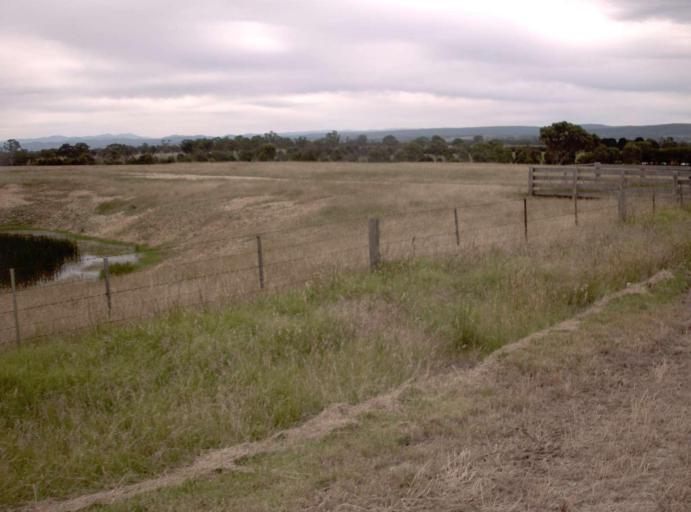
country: AU
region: Victoria
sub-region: East Gippsland
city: Bairnsdale
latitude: -37.8729
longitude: 147.5607
